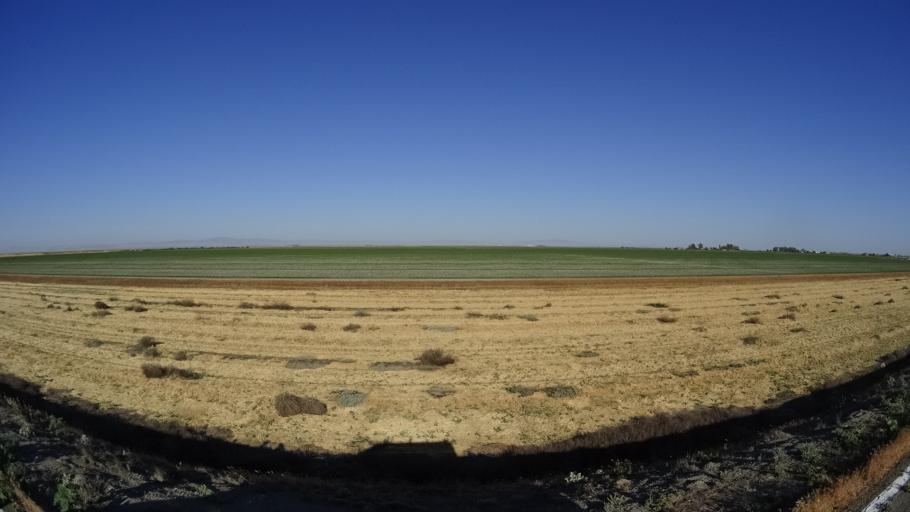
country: US
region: California
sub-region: Kings County
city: Stratford
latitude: 36.1446
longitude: -119.7980
